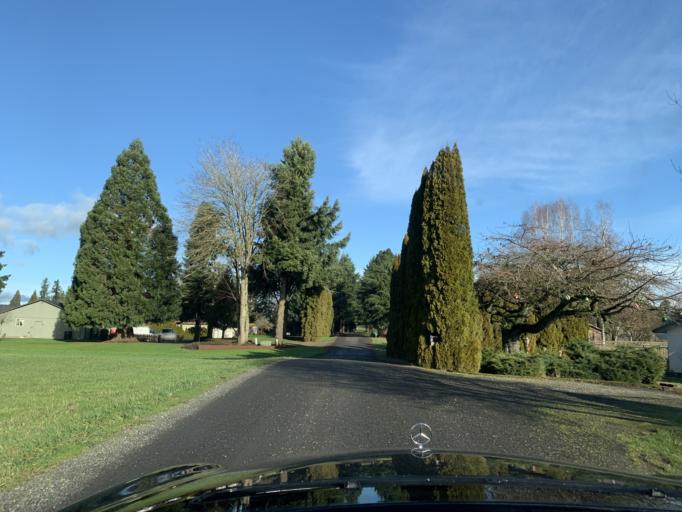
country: US
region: Washington
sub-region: Clark County
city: Five Corners
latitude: 45.7083
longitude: -122.5738
